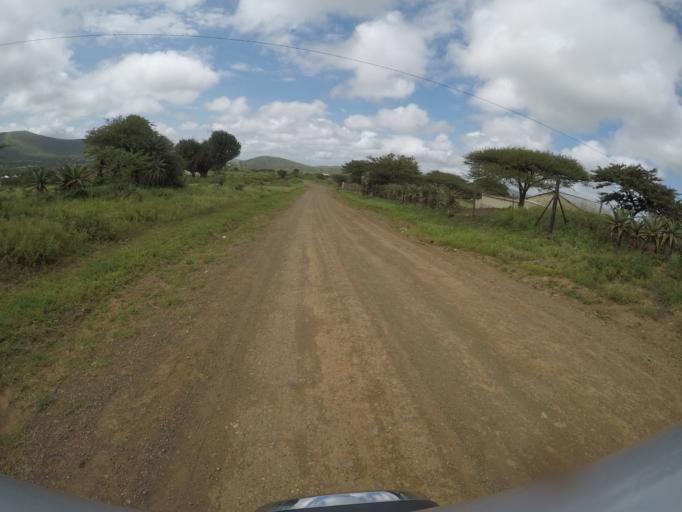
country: ZA
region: KwaZulu-Natal
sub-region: uThungulu District Municipality
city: Empangeni
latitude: -28.5797
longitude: 31.8492
